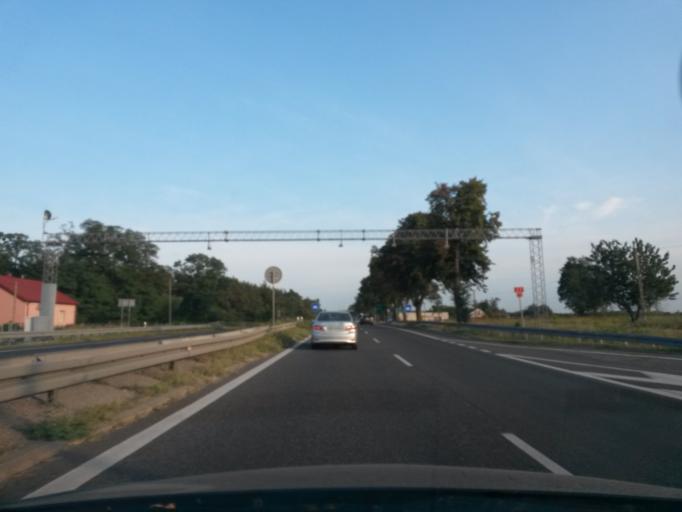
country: PL
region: Masovian Voivodeship
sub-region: Powiat nowodworski
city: Zakroczym
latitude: 52.4612
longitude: 20.5759
